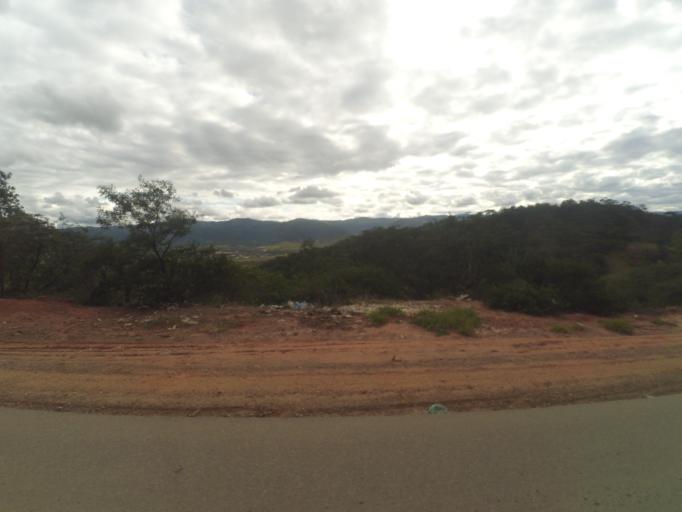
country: BO
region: Santa Cruz
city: Samaipata
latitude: -18.1644
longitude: -63.9056
